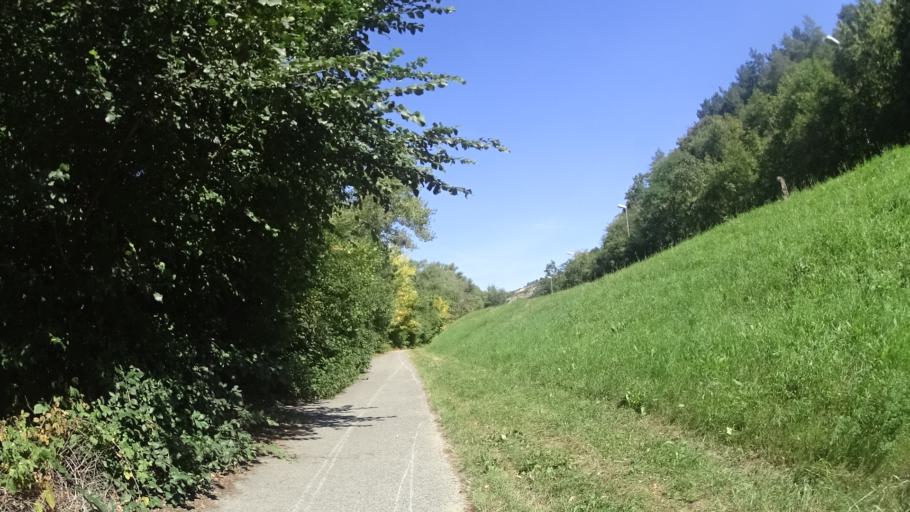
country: AT
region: Lower Austria
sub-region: Politischer Bezirk Bruck an der Leitha
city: Hainburg an der Donau
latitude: 48.1856
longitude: 16.9776
